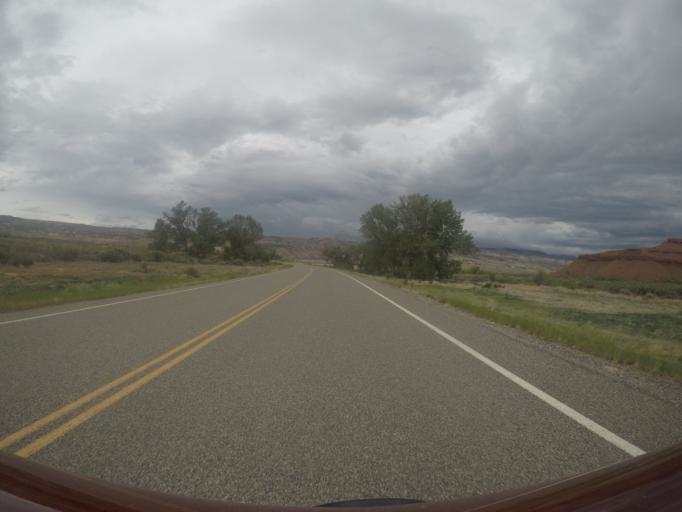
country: US
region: Wyoming
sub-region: Big Horn County
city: Lovell
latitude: 44.9647
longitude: -108.2766
